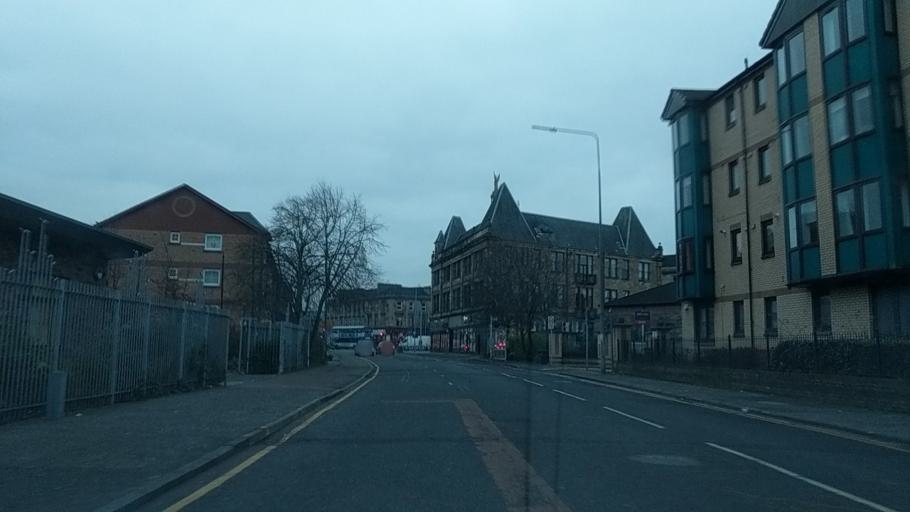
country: GB
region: Scotland
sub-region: Glasgow City
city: Glasgow
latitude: 55.8545
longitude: -4.2808
